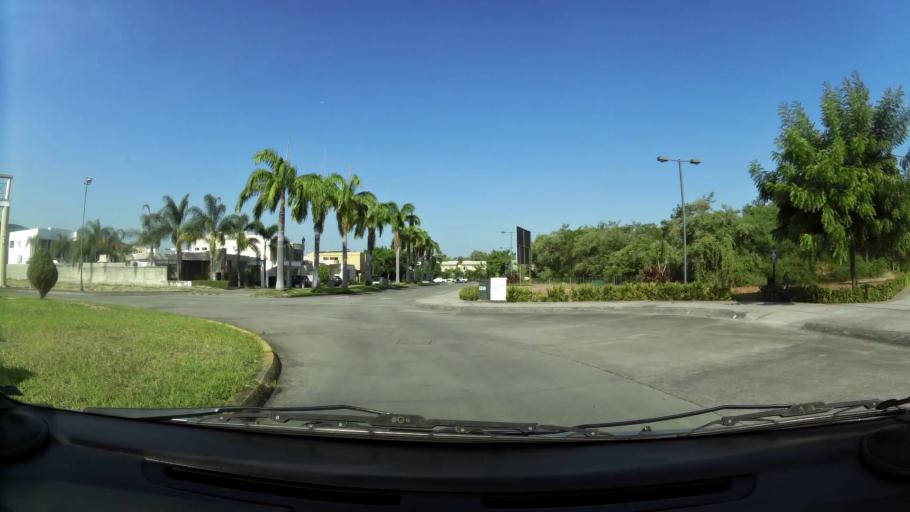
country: EC
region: Guayas
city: Santa Lucia
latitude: -2.1880
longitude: -79.9866
